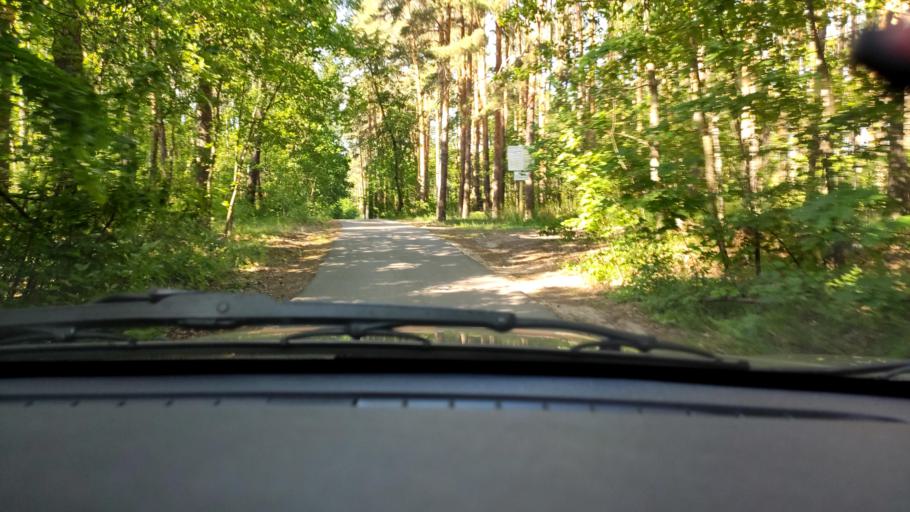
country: RU
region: Voronezj
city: Somovo
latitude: 51.8055
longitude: 39.3818
